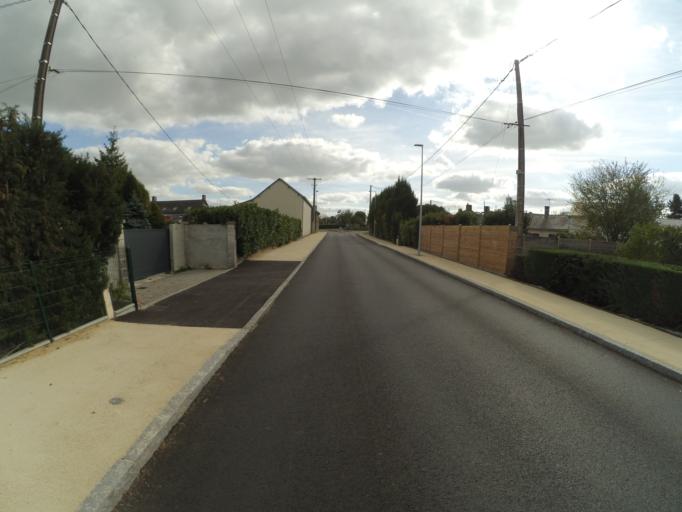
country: FR
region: Pays de la Loire
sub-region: Departement de la Loire-Atlantique
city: Carquefou
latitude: 47.3056
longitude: -1.5039
